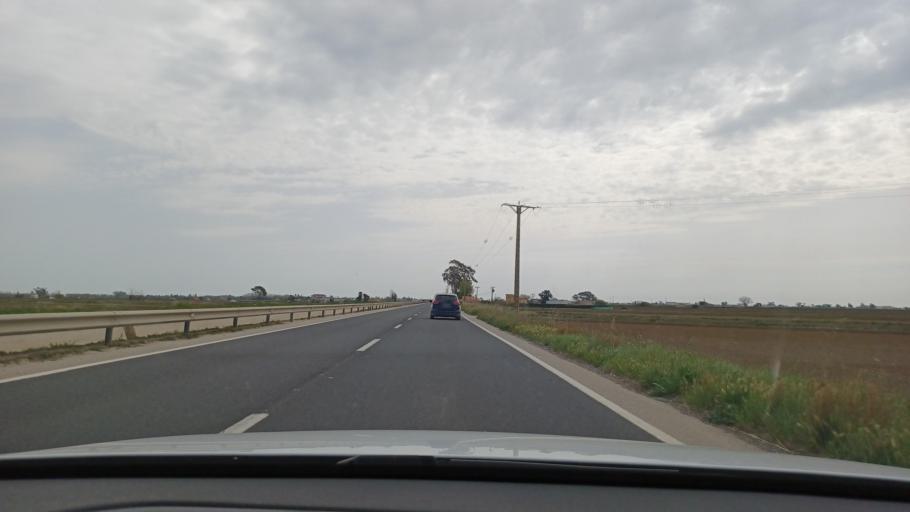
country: ES
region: Catalonia
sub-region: Provincia de Tarragona
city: Deltebre
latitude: 40.7099
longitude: 0.6524
